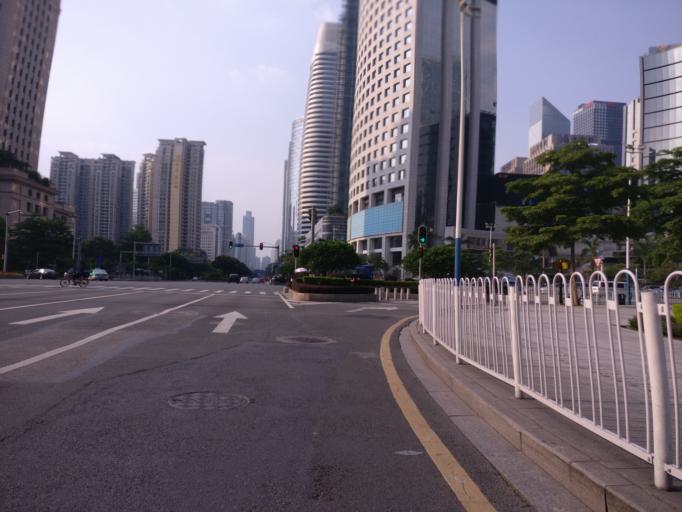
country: CN
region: Guangdong
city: Wushan
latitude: 23.1214
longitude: 113.3160
